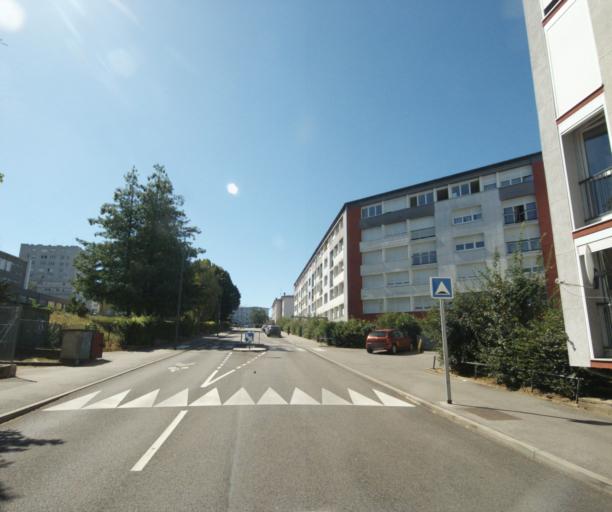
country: FR
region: Lorraine
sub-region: Departement des Vosges
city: Epinal
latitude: 48.1851
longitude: 6.4538
